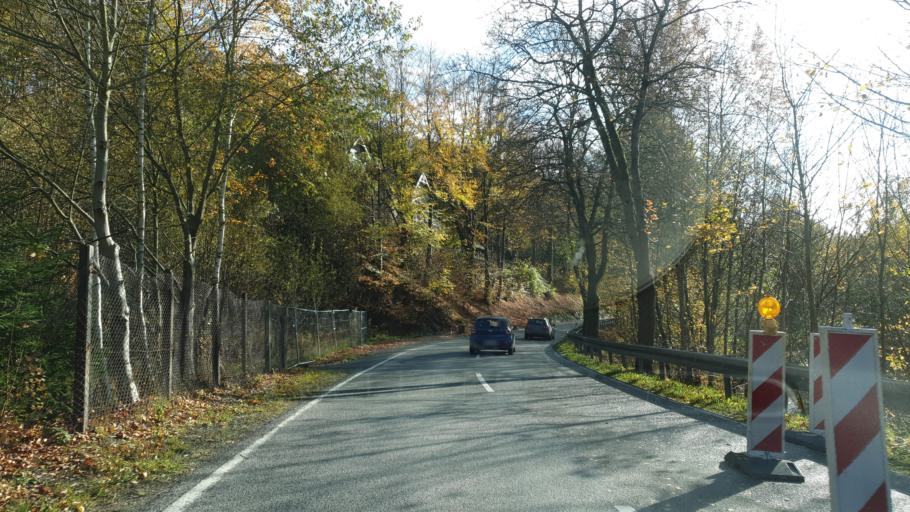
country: DE
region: Saxony
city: Aue
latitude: 50.5760
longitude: 12.6909
